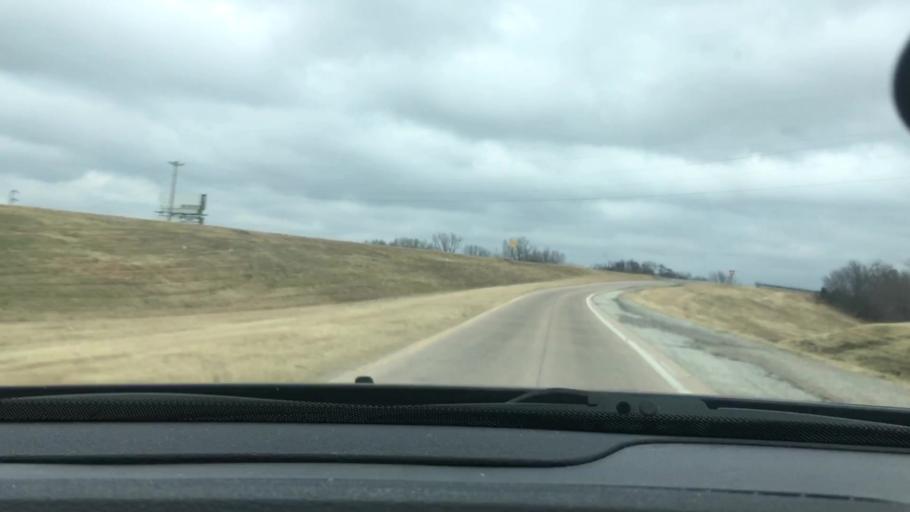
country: US
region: Oklahoma
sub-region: Bryan County
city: Durant
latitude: 34.0373
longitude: -96.3743
